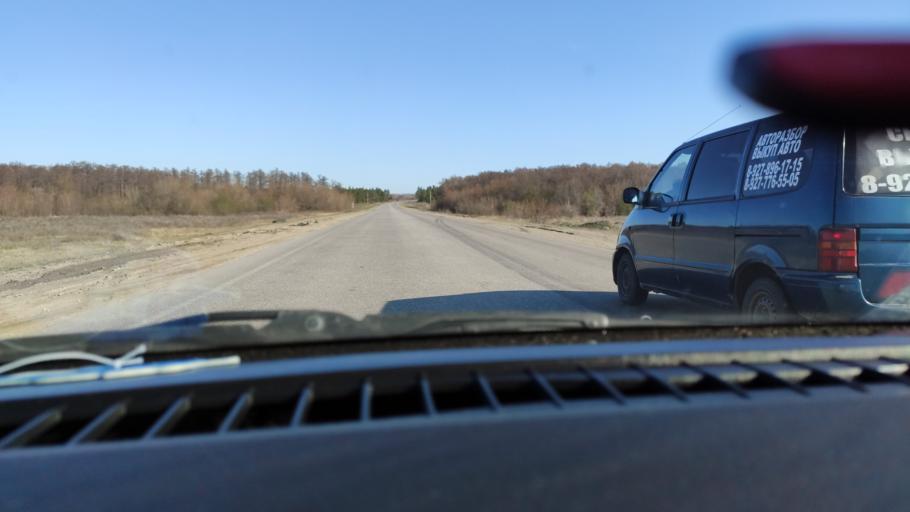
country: RU
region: Samara
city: Varlamovo
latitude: 53.1426
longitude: 48.2854
